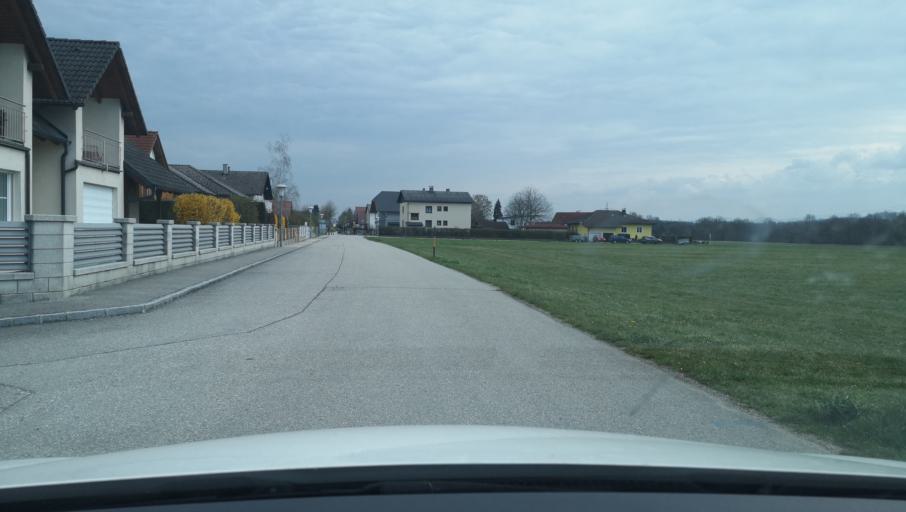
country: AT
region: Lower Austria
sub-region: Politischer Bezirk Amstetten
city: Euratsfeld
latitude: 48.1124
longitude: 14.9108
